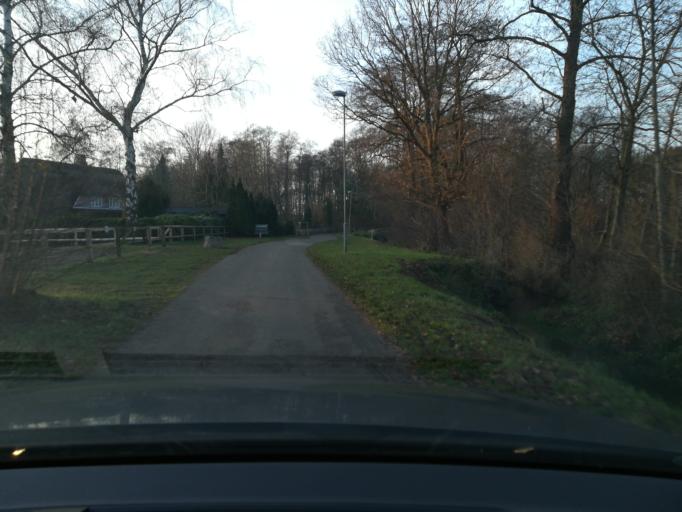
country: DE
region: Schleswig-Holstein
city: Escheburg
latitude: 53.4502
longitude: 10.3003
